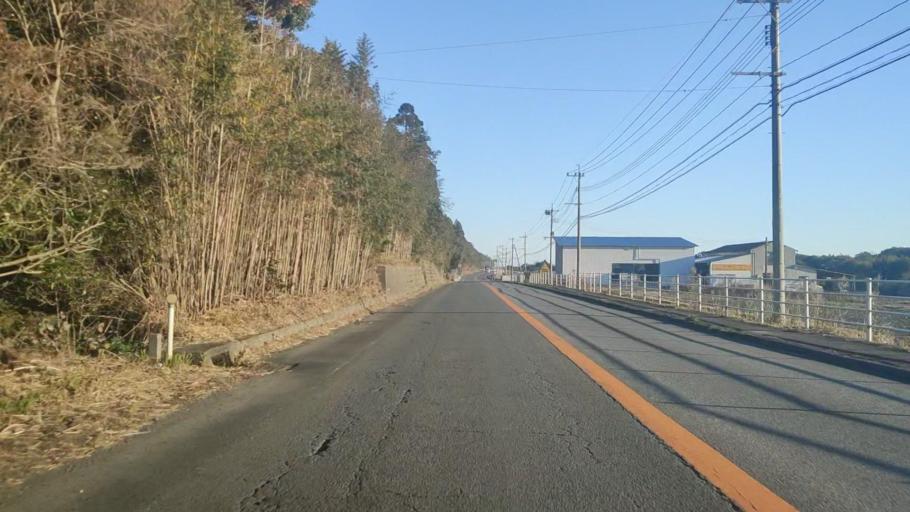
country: JP
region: Miyazaki
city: Takanabe
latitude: 32.0981
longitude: 131.5188
